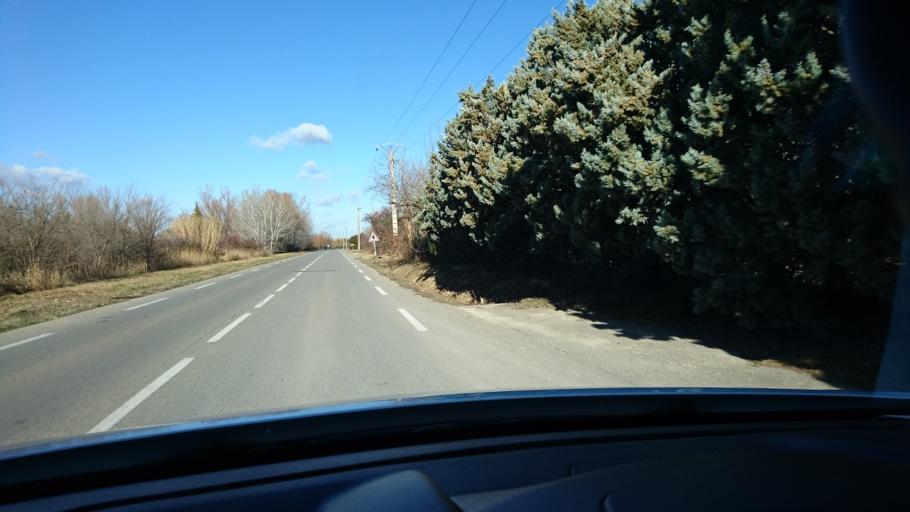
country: FR
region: Provence-Alpes-Cote d'Azur
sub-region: Departement du Vaucluse
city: Morieres-les-Avignon
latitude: 43.9197
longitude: 4.9060
